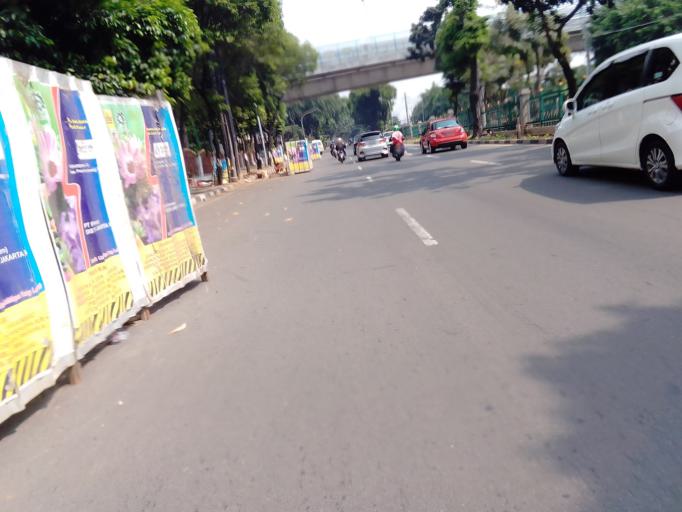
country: ID
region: Jakarta Raya
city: Jakarta
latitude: -6.2227
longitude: 106.7906
